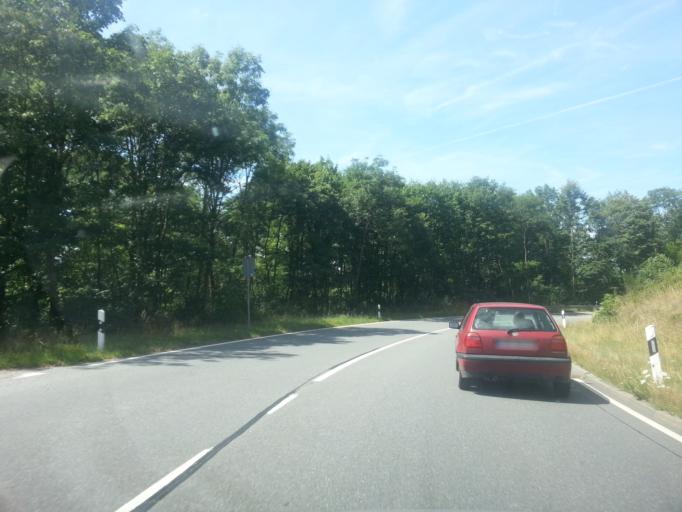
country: DE
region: Hesse
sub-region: Regierungsbezirk Darmstadt
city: Lindenfels
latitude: 49.7019
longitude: 8.7574
